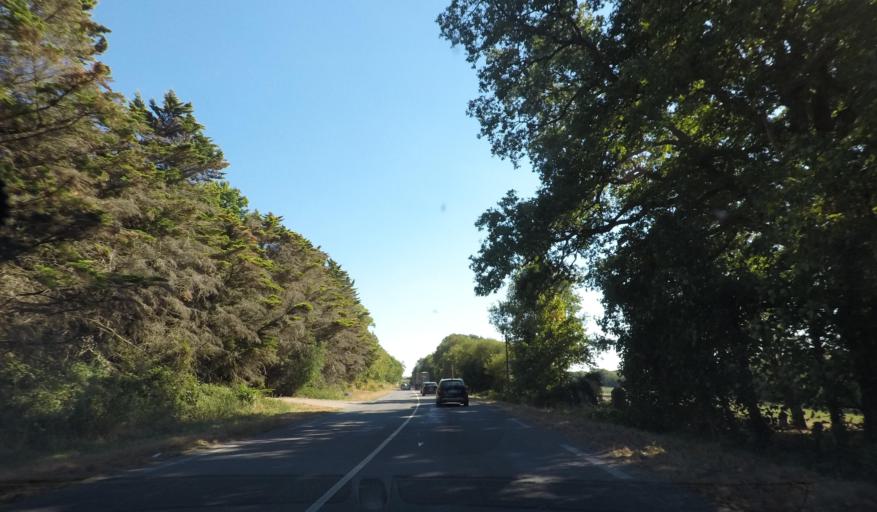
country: FR
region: Pays de la Loire
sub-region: Departement de la Loire-Atlantique
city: Pontchateau
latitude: 47.4207
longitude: -2.0913
